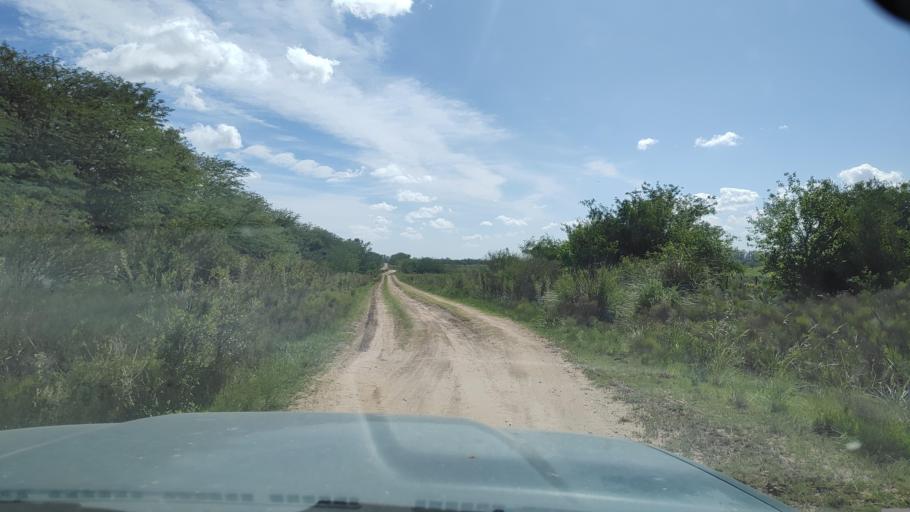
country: AR
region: Buenos Aires
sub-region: Partido de Lujan
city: Lujan
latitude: -34.5227
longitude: -59.1715
